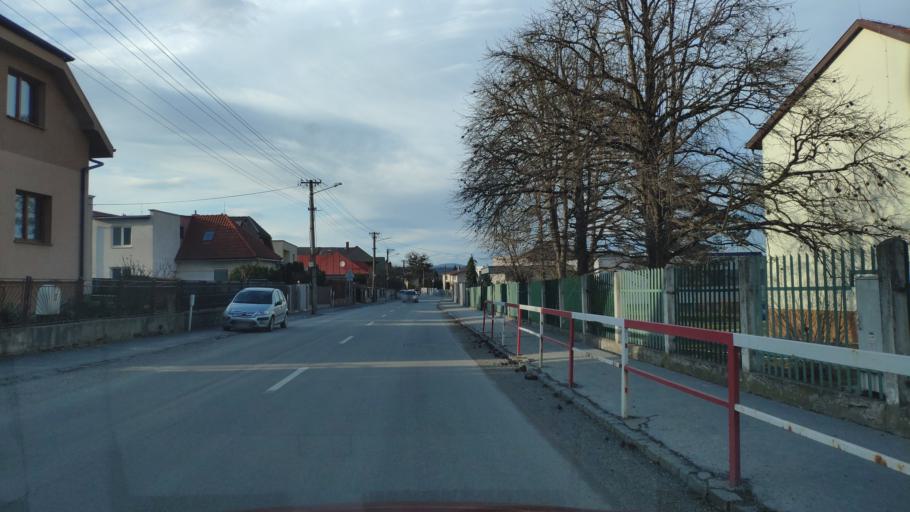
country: SK
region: Kosicky
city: Kosice
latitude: 48.6796
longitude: 21.2631
